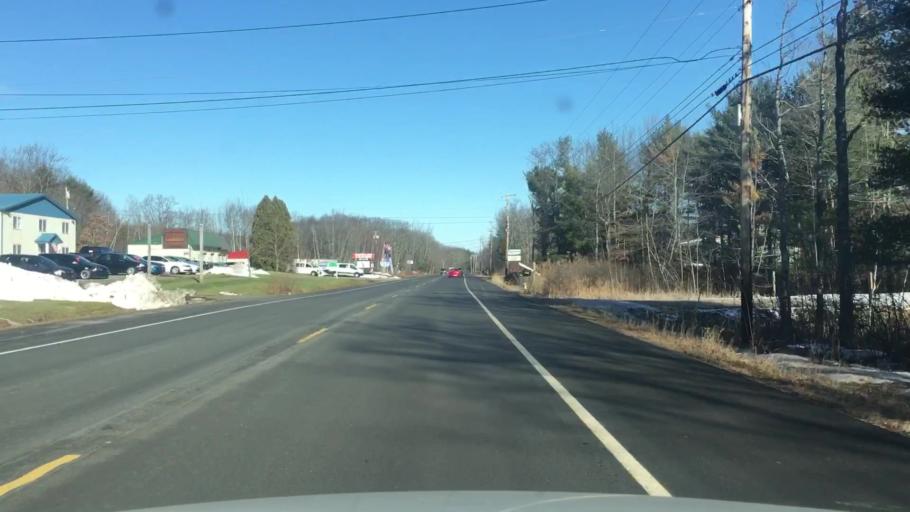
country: US
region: Maine
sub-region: York County
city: Arundel
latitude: 43.4390
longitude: -70.5033
